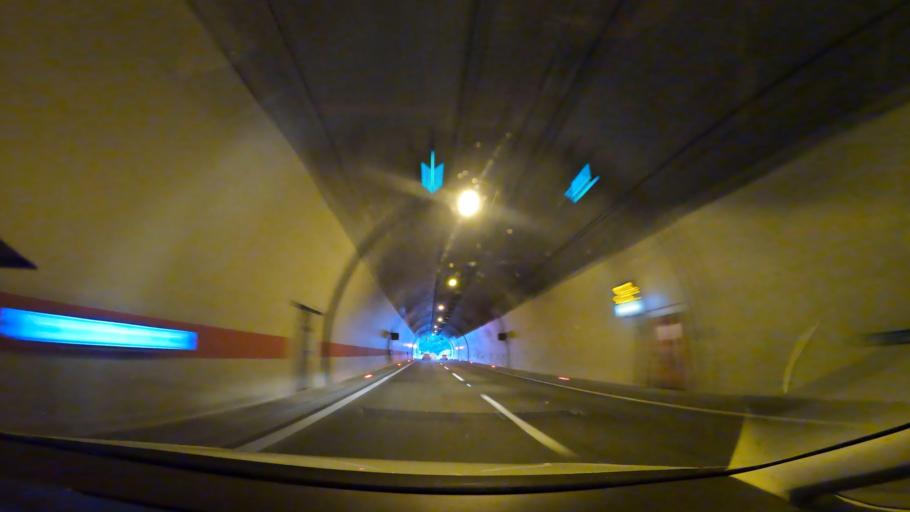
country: HR
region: Primorsko-Goranska
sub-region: Grad Delnice
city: Delnice
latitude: 45.3439
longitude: 14.7472
